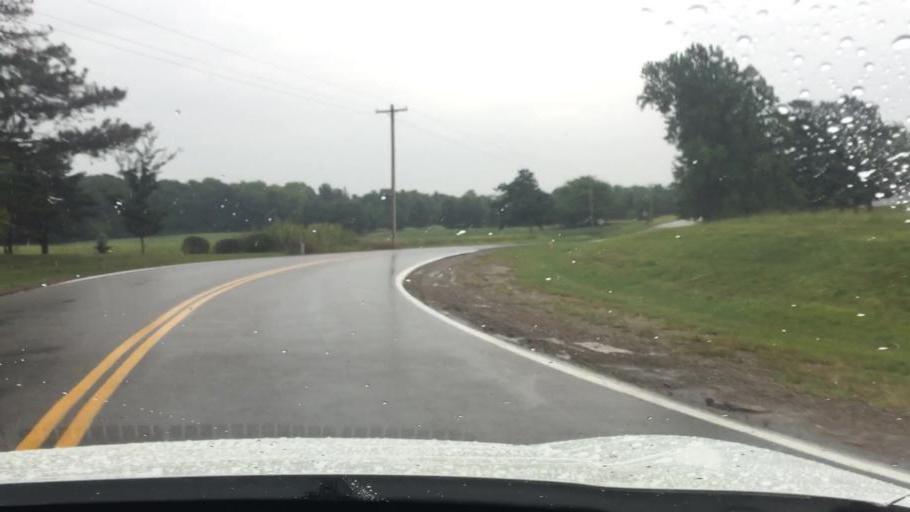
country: US
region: Ohio
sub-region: Champaign County
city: Urbana
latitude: 40.0940
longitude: -83.7328
